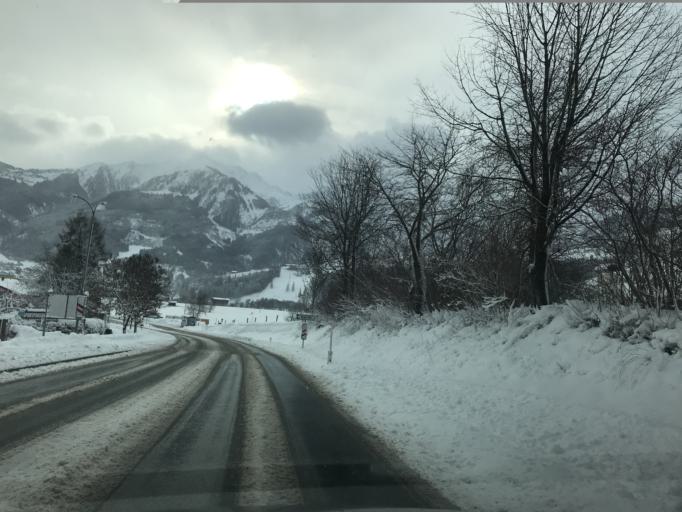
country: AT
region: Salzburg
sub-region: Politischer Bezirk Zell am See
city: Kaprun
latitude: 47.2896
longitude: 12.7454
